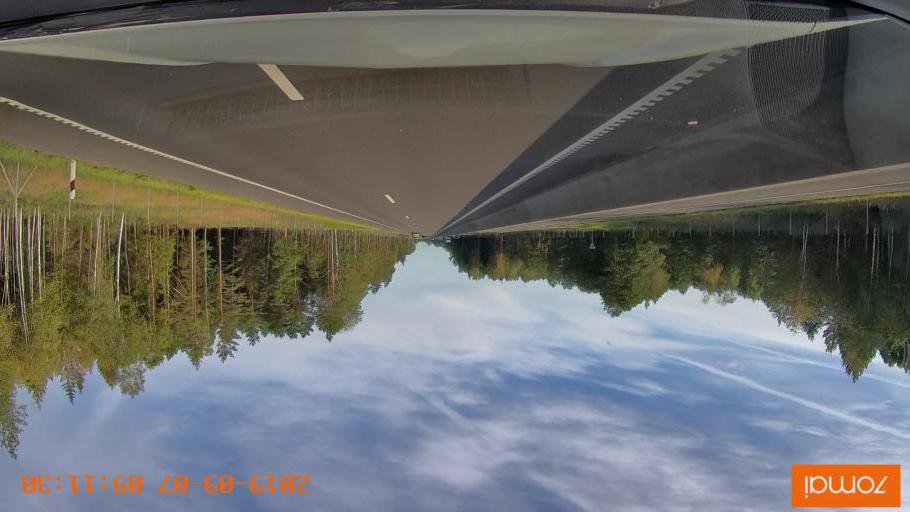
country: BY
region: Minsk
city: Valozhyn
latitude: 54.0325
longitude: 26.4505
